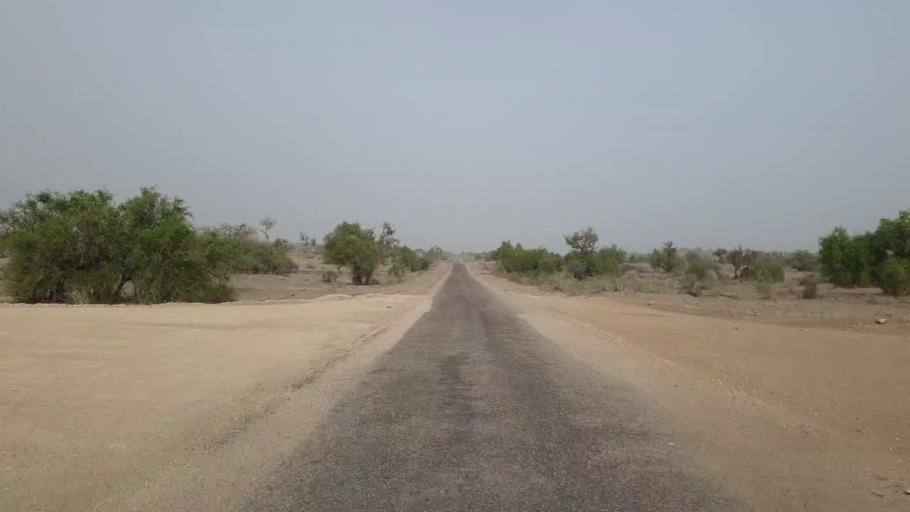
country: PK
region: Sindh
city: Islamkot
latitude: 24.5660
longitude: 70.3307
